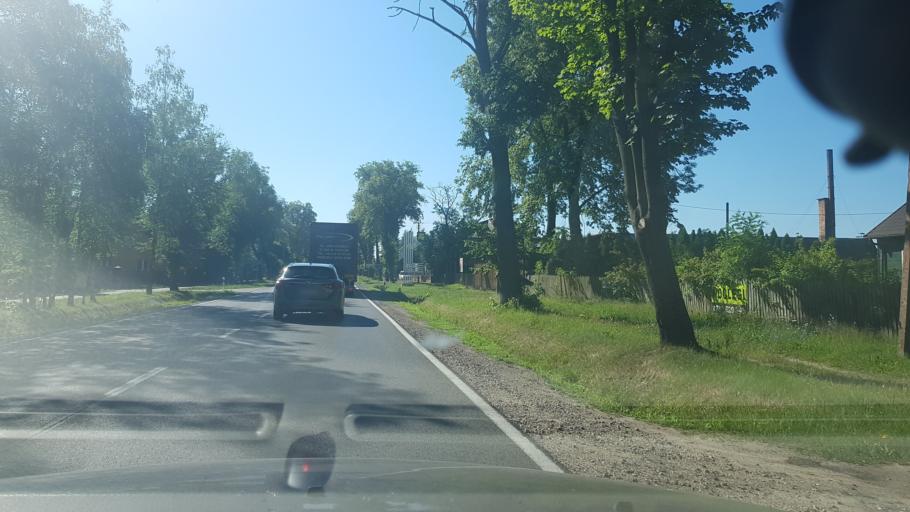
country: PL
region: Masovian Voivodeship
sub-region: Powiat wegrowski
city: Lochow
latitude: 52.5364
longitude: 21.6720
